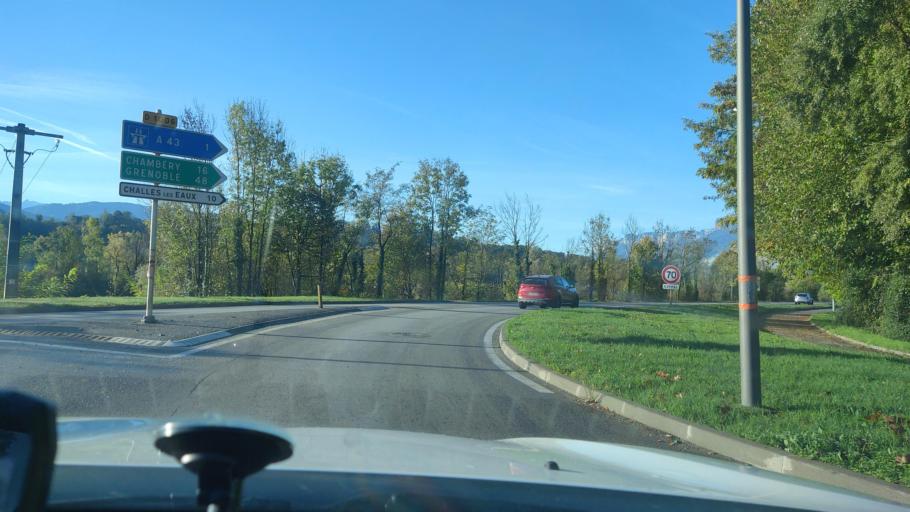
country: FR
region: Rhone-Alpes
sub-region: Departement de la Savoie
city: Montmelian
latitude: 45.5021
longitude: 6.0676
